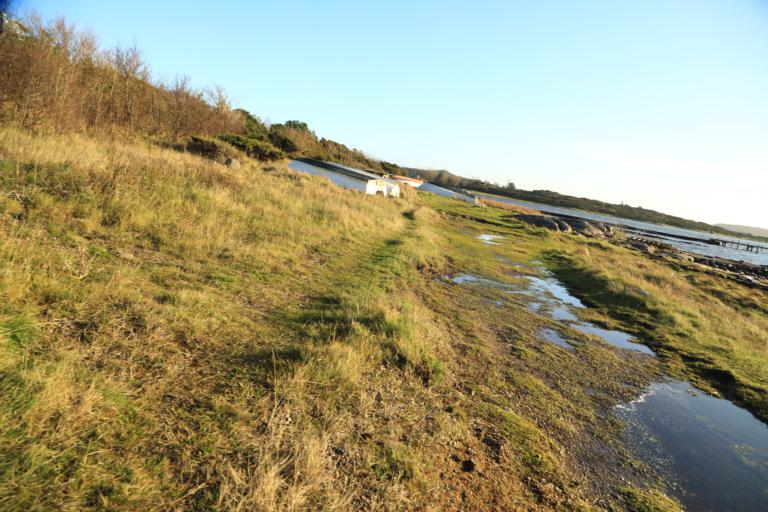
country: SE
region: Halland
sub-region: Varbergs Kommun
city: Varberg
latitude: 57.1680
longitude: 12.2119
